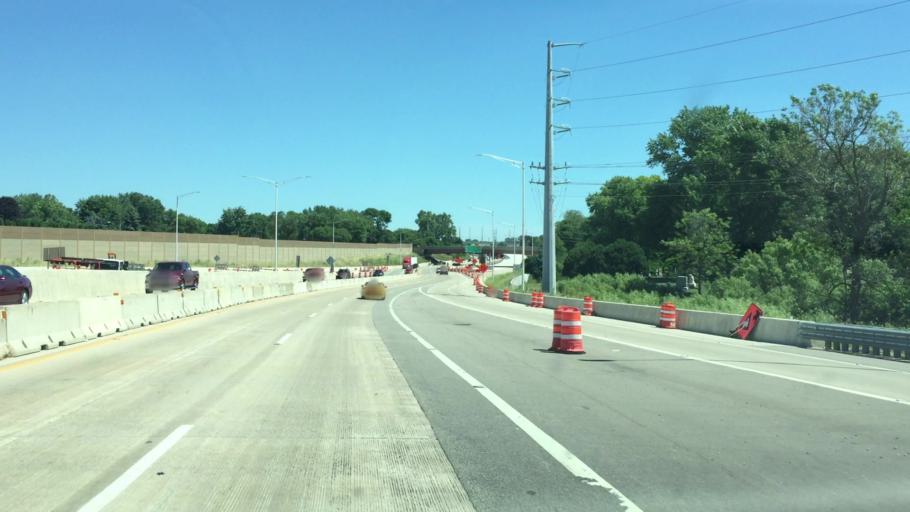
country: US
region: Wisconsin
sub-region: Winnebago County
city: Menasha
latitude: 44.2225
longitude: -88.4473
